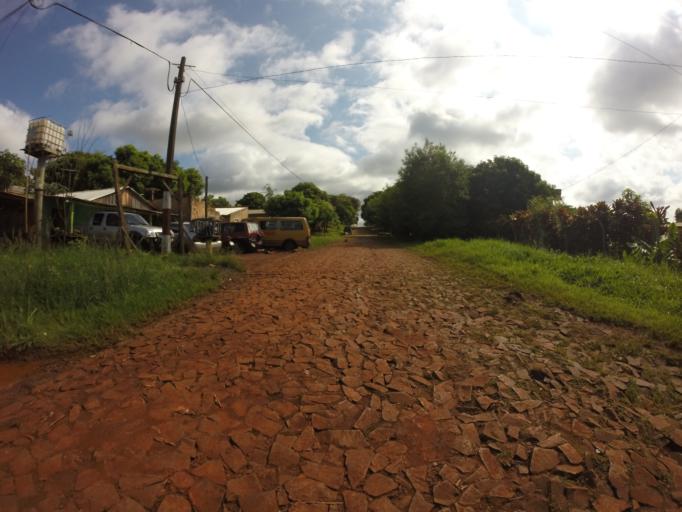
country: PY
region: Alto Parana
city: Ciudad del Este
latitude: -25.3934
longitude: -54.6448
